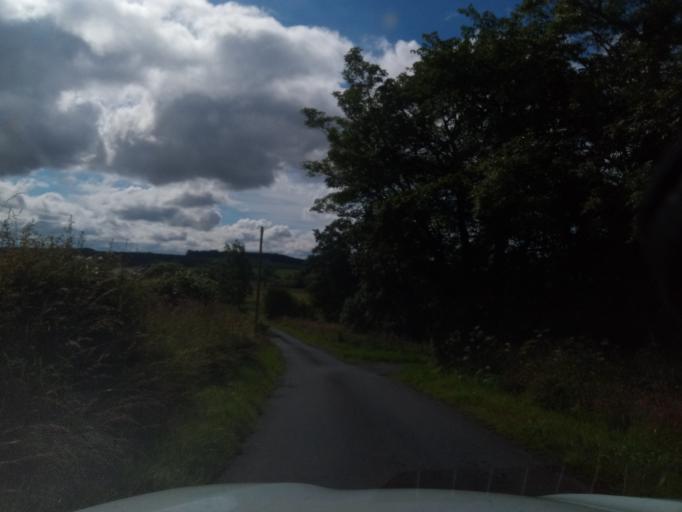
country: GB
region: Scotland
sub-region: The Scottish Borders
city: Saint Boswells
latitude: 55.6081
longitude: -2.6104
